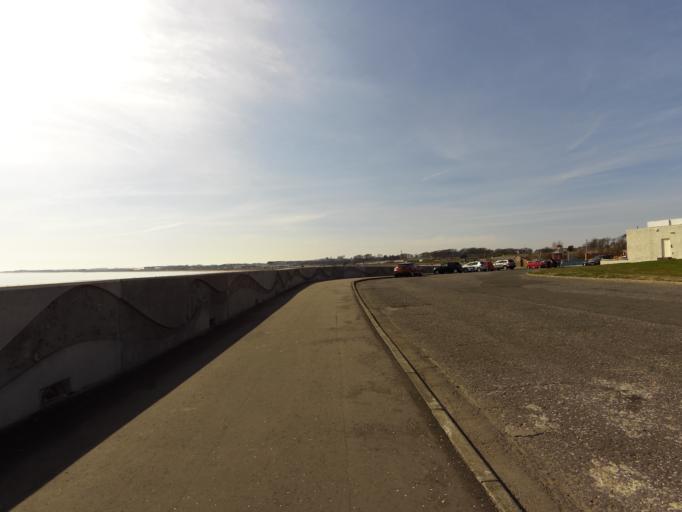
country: GB
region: Scotland
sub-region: Angus
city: Arbroath
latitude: 56.5512
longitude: -2.5967
